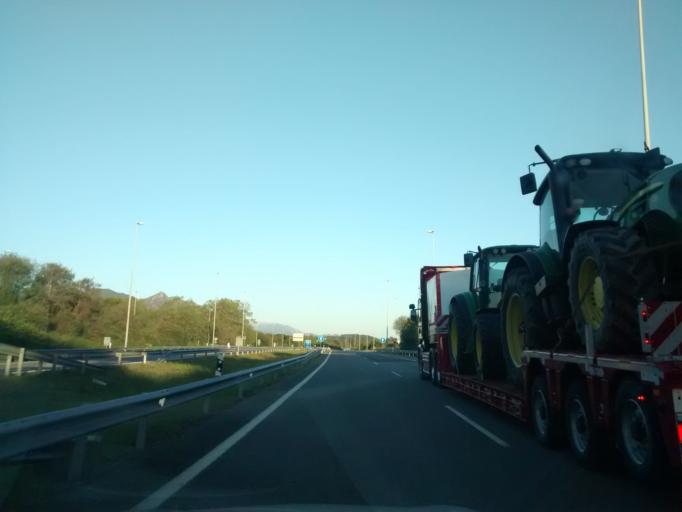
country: ES
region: Asturias
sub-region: Province of Asturias
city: Carrena
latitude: 43.4442
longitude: -4.8872
